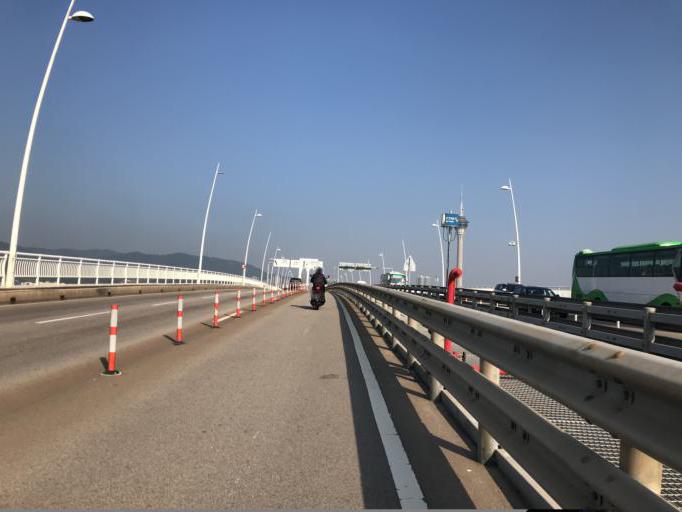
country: MO
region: Macau
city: Macau
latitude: 22.1659
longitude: 113.5394
